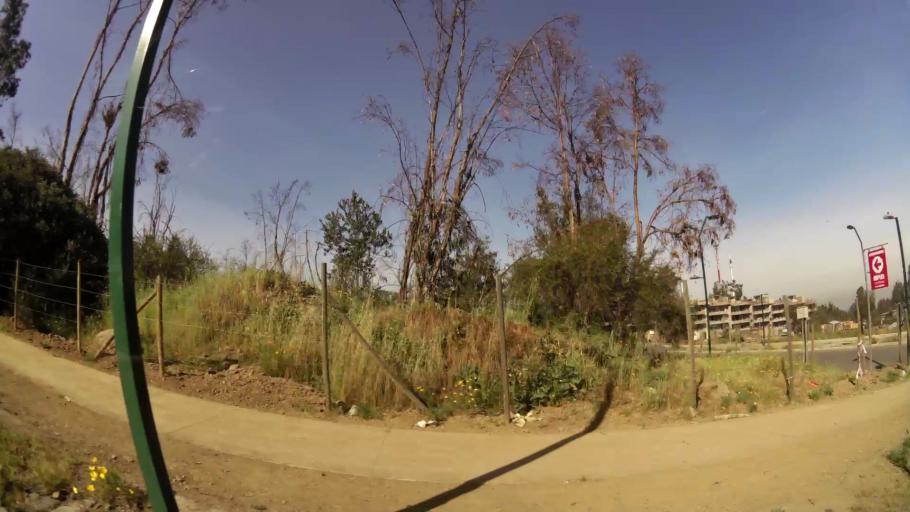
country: CL
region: Santiago Metropolitan
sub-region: Provincia de Santiago
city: Villa Presidente Frei, Nunoa, Santiago, Chile
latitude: -33.4951
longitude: -70.5300
